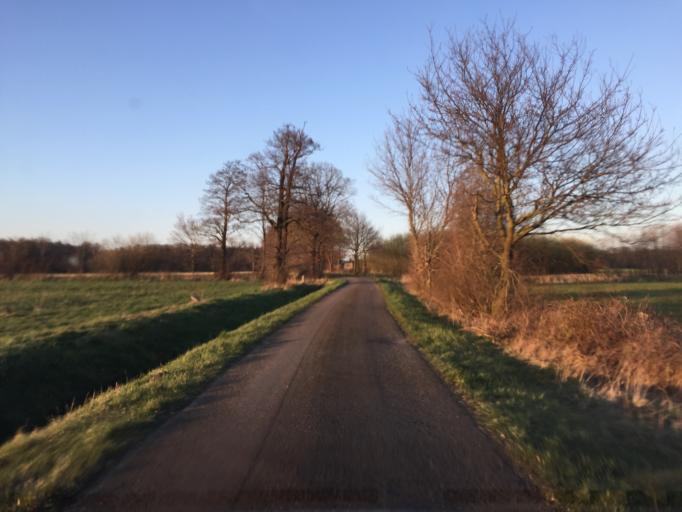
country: DE
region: Lower Saxony
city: Varrel
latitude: 52.6622
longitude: 8.7474
